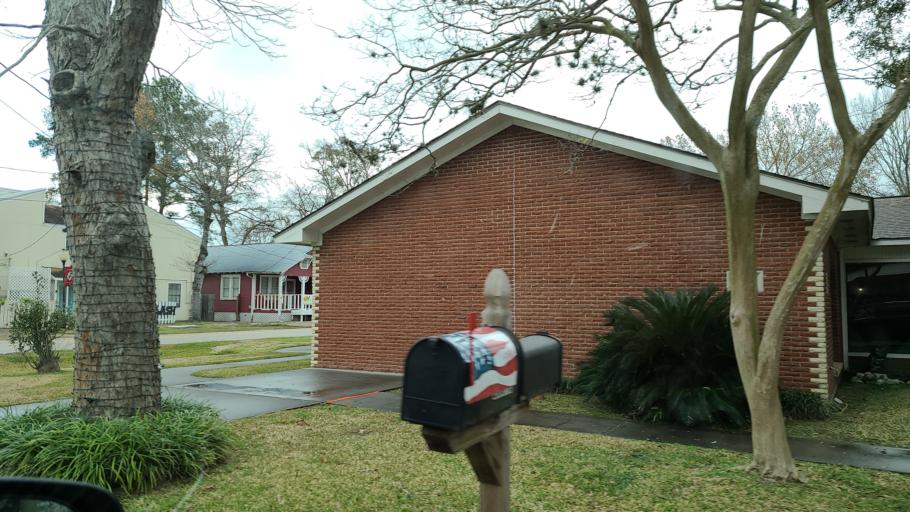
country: US
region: Texas
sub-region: Harris County
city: Spring
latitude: 30.0799
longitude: -95.4200
